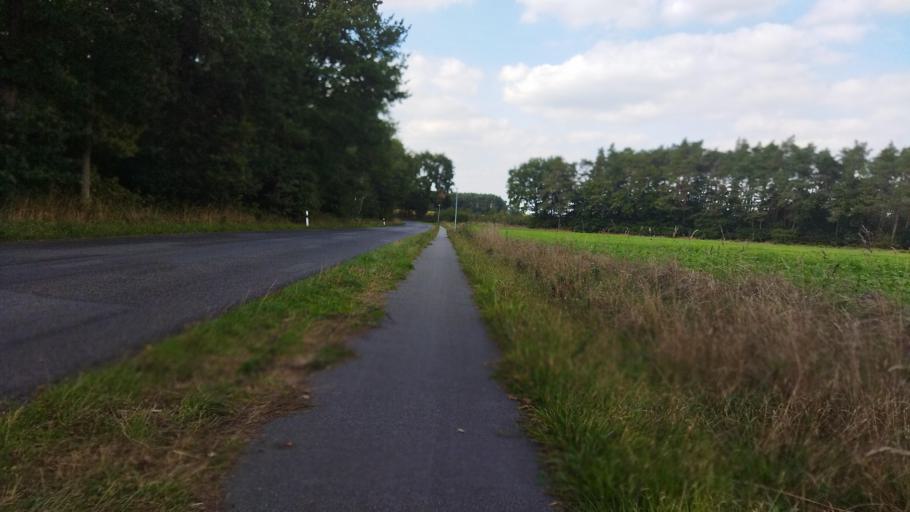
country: DE
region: Lower Saxony
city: Haren
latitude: 52.8072
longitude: 7.2689
